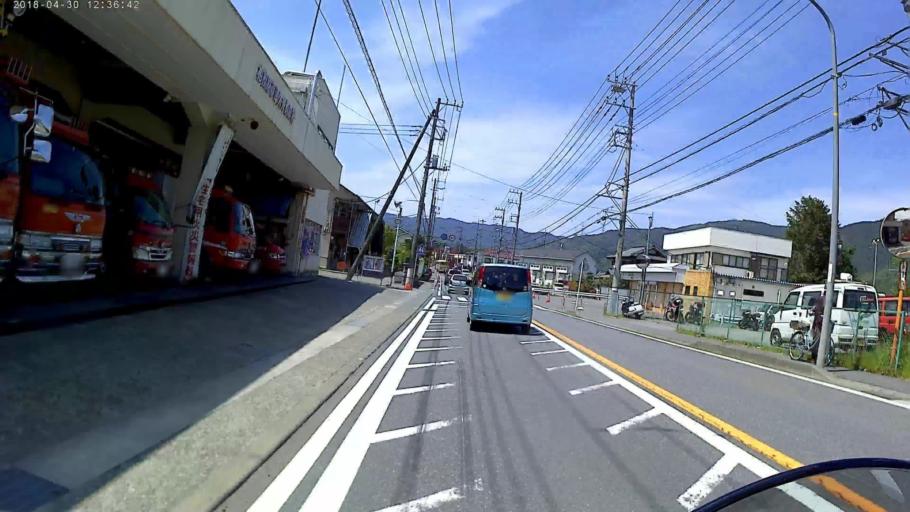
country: JP
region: Yamanashi
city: Uenohara
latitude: 35.5990
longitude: 139.2252
